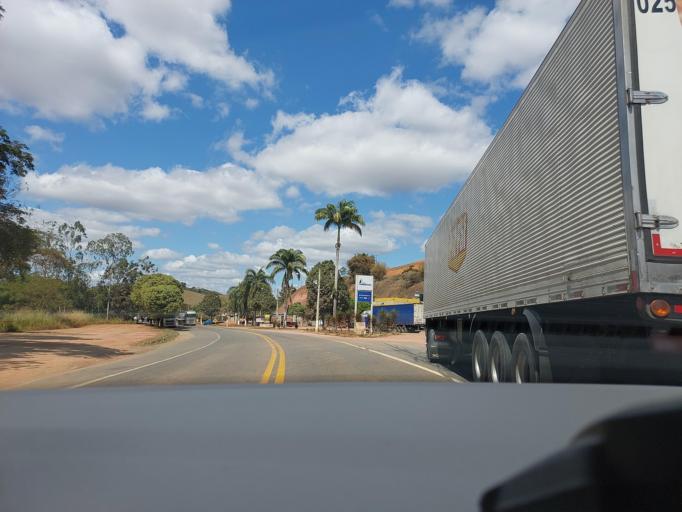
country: BR
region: Minas Gerais
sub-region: Muriae
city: Muriae
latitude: -21.1257
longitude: -42.2034
